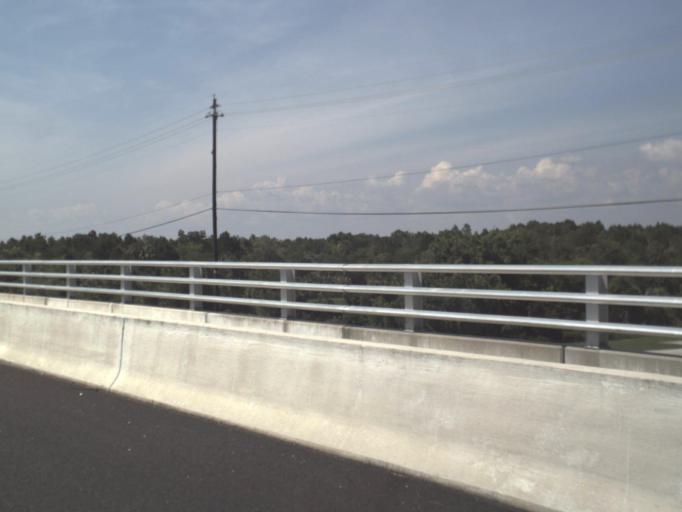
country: US
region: Florida
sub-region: Levy County
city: Inglis
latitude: 29.0119
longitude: -82.6628
